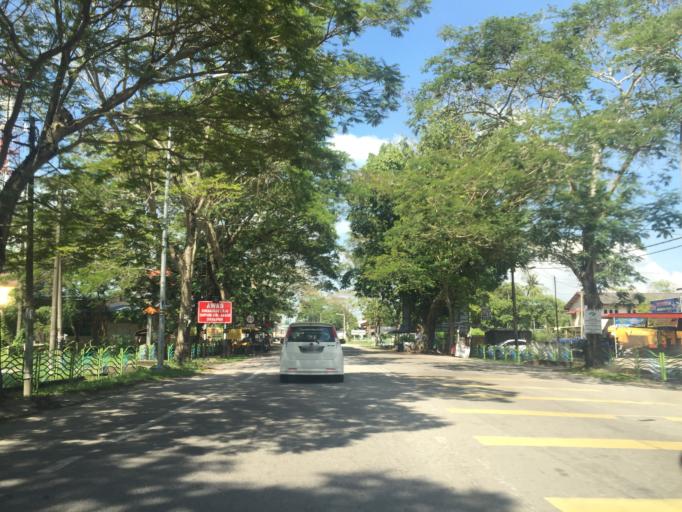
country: MY
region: Penang
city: Tasek Glugor
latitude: 5.4817
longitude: 100.4945
